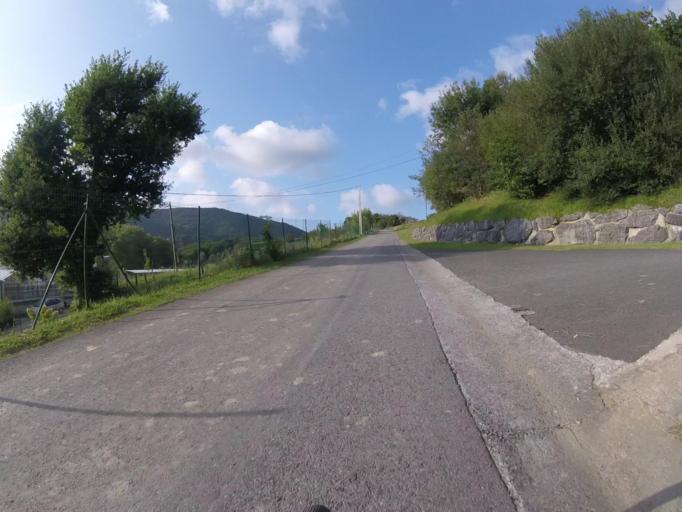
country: ES
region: Basque Country
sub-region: Provincia de Guipuzcoa
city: Irun
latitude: 43.3473
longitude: -1.8195
